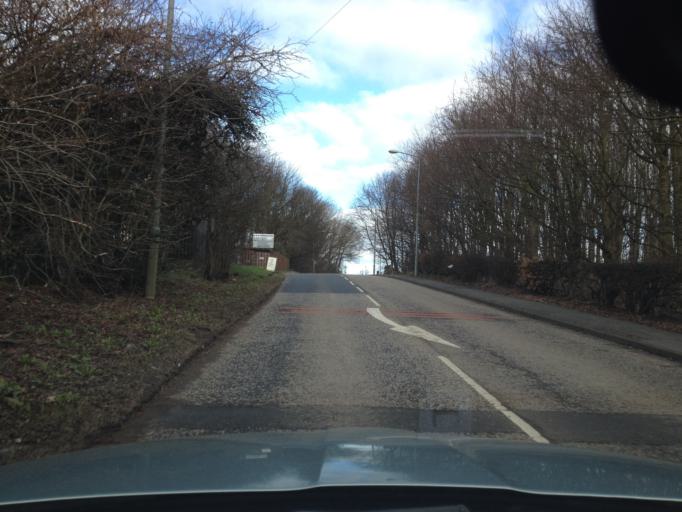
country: GB
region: Scotland
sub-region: West Lothian
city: Mid Calder
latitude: 55.9037
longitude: -3.4893
